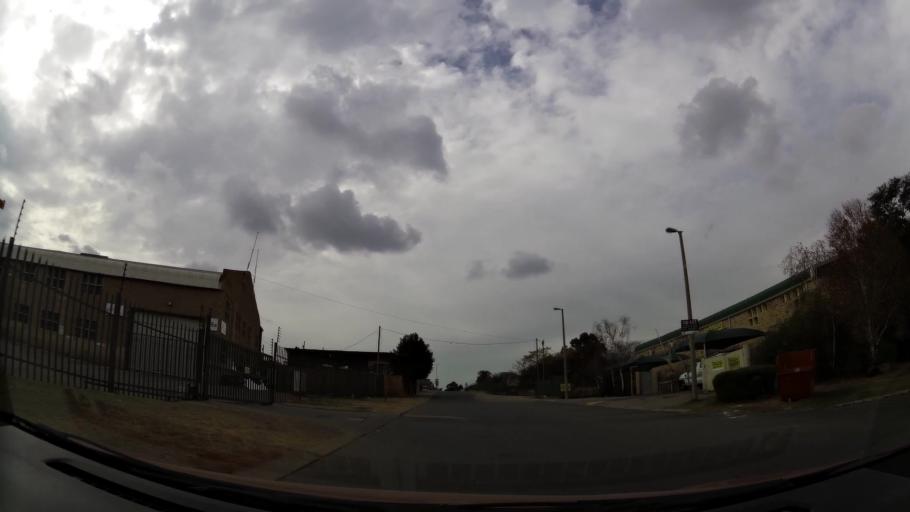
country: ZA
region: Gauteng
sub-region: West Rand District Municipality
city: Muldersdriseloop
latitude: -26.0749
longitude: 27.9129
